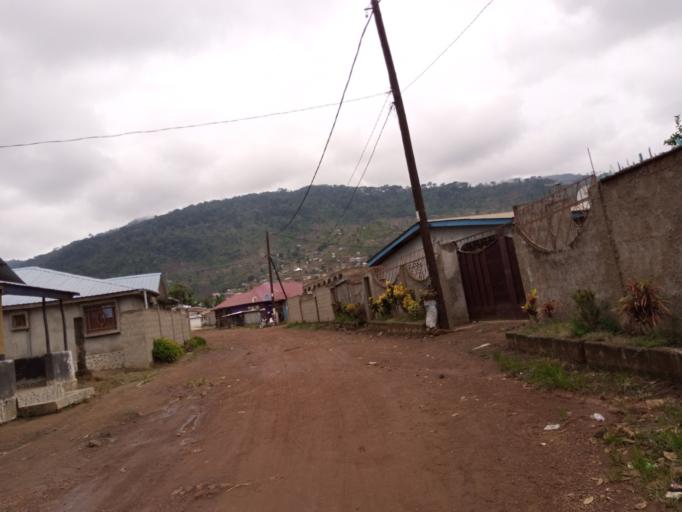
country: SL
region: Western Area
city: Hastings
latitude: 8.3799
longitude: -13.1523
